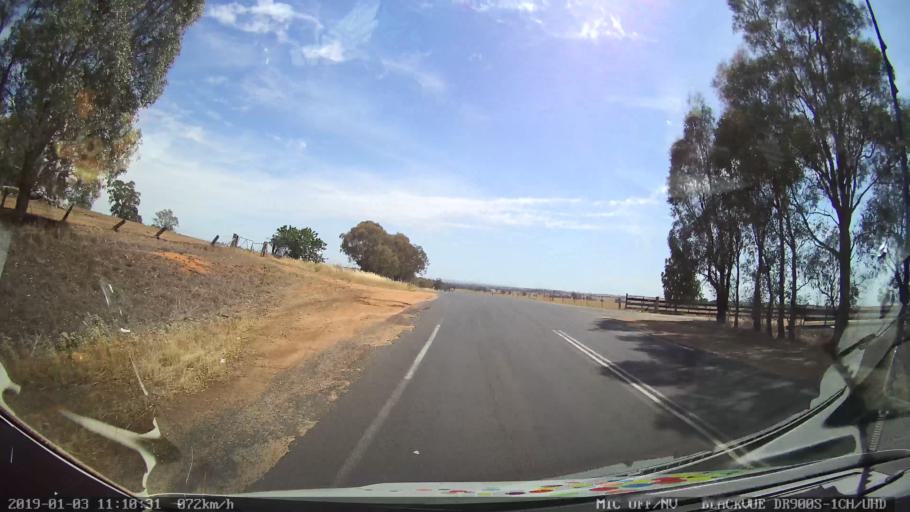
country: AU
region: New South Wales
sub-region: Young
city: Young
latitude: -34.2260
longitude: 148.2588
